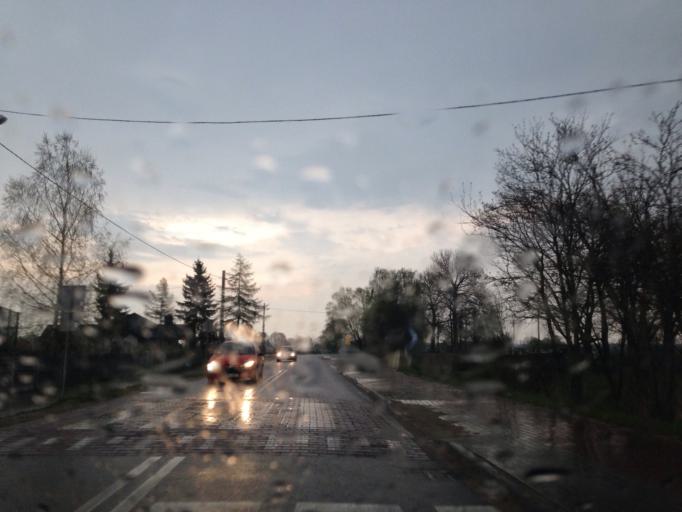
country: PL
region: Masovian Voivodeship
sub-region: Powiat plonski
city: Baboszewo
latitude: 52.7042
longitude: 20.2171
